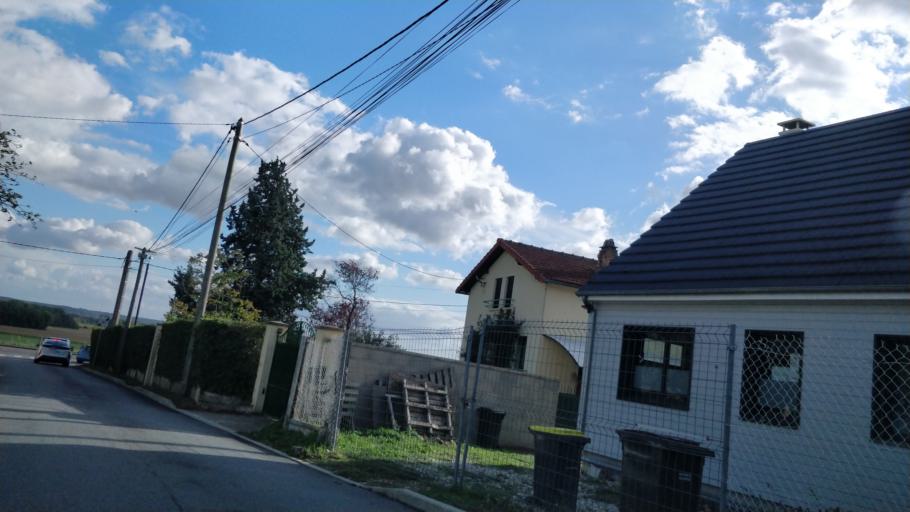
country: FR
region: Ile-de-France
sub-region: Departement de l'Essonne
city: Fontenay-les-Briis
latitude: 48.6199
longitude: 2.1505
